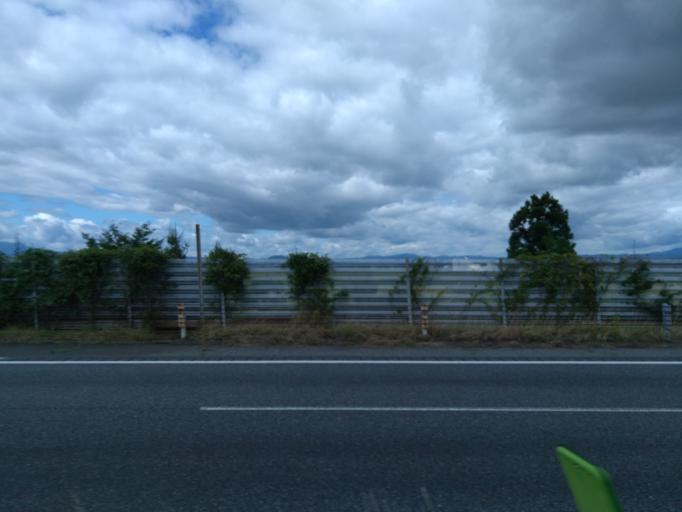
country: JP
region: Miyagi
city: Furukawa
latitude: 38.5750
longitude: 140.9284
